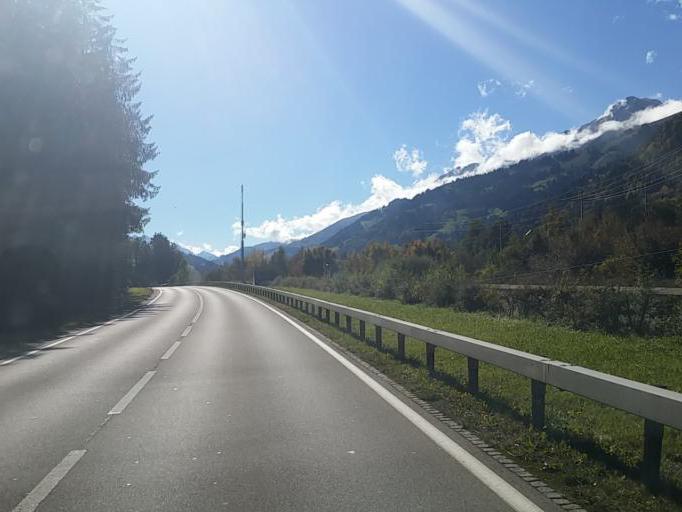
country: CH
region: Bern
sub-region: Frutigen-Niedersimmental District
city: Frutigen
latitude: 46.6042
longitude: 7.6633
